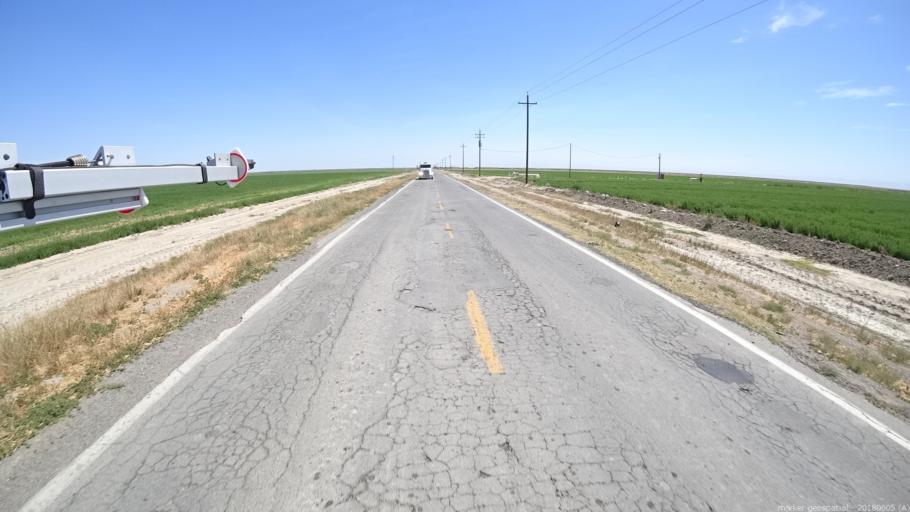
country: US
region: California
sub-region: Fresno County
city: Firebaugh
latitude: 37.0052
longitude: -120.3833
